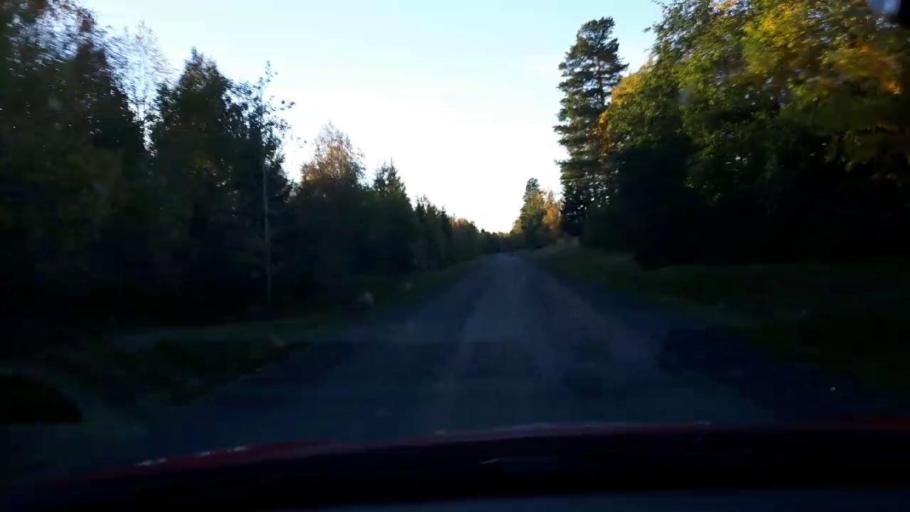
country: SE
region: Jaemtland
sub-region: Krokoms Kommun
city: Krokom
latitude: 63.4456
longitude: 14.5831
